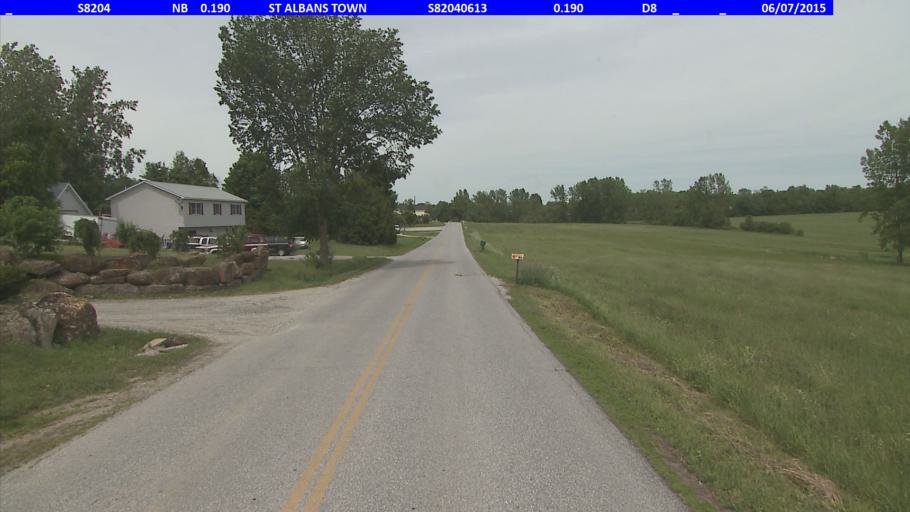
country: US
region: Vermont
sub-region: Franklin County
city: Saint Albans
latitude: 44.8055
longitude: -73.1120
